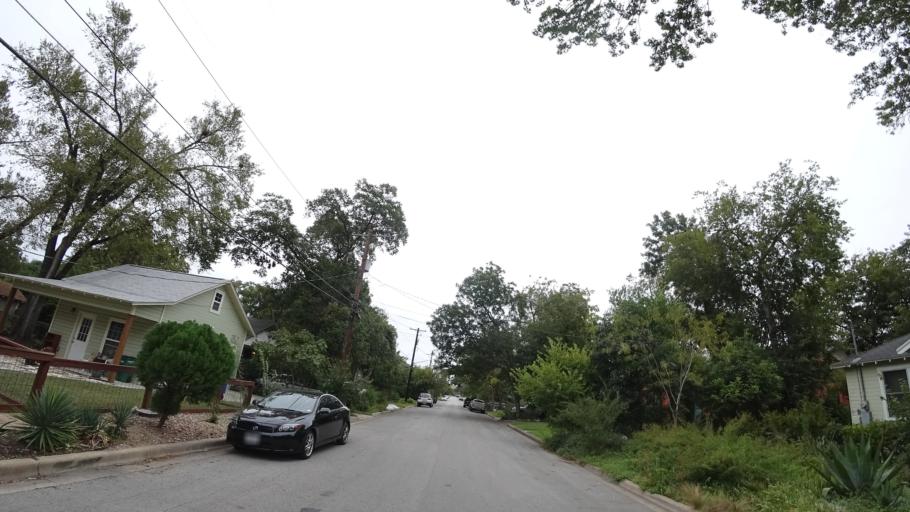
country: US
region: Texas
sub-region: Travis County
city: Austin
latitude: 30.2968
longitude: -97.7220
